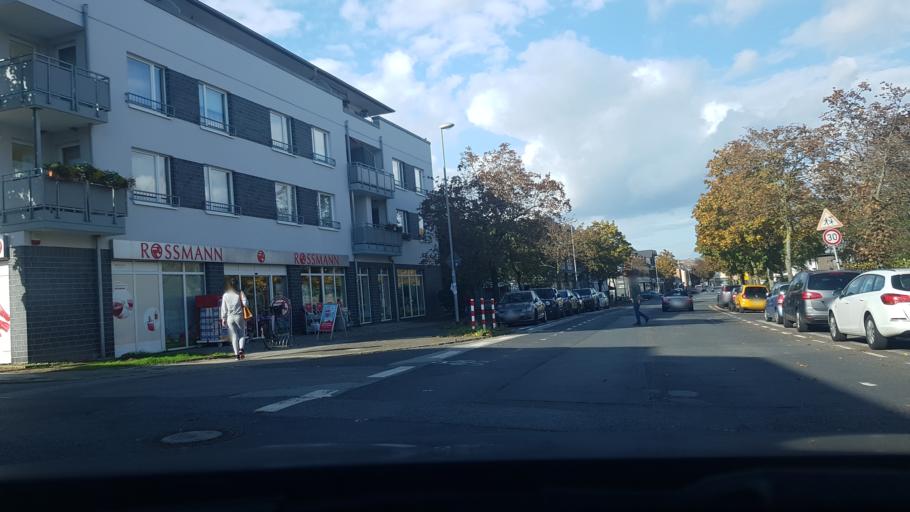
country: DE
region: North Rhine-Westphalia
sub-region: Regierungsbezirk Dusseldorf
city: Moers
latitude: 51.4152
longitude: 6.5943
